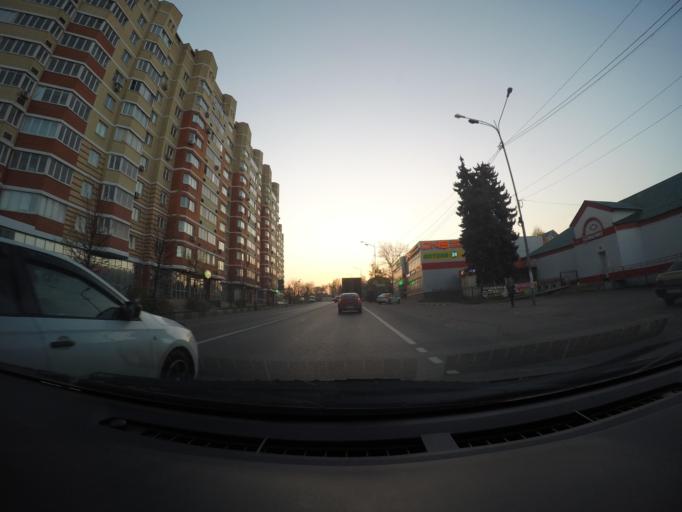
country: RU
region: Moskovskaya
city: Kraskovo
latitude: 55.6579
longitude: 37.9821
